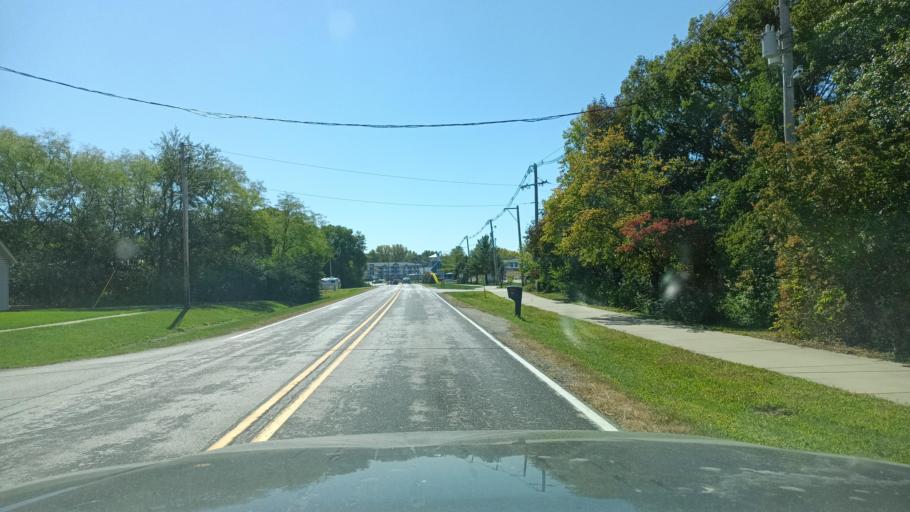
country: US
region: Illinois
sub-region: Champaign County
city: Mahomet
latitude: 40.1920
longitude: -88.3914
